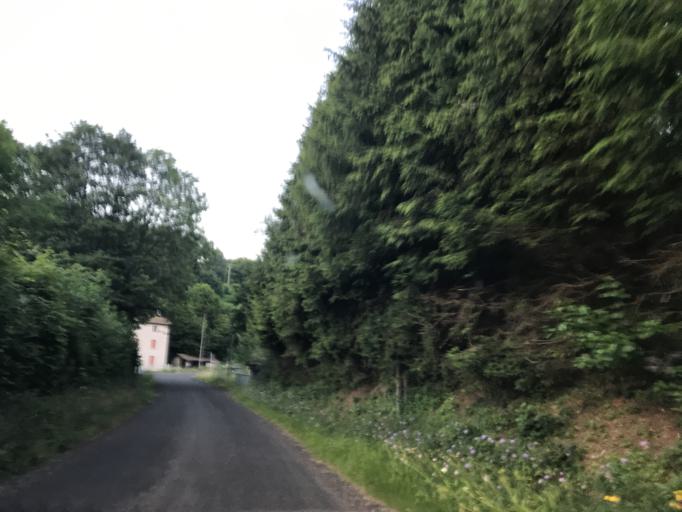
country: FR
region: Rhone-Alpes
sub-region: Departement de la Loire
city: Noiretable
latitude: 45.7675
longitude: 3.6959
